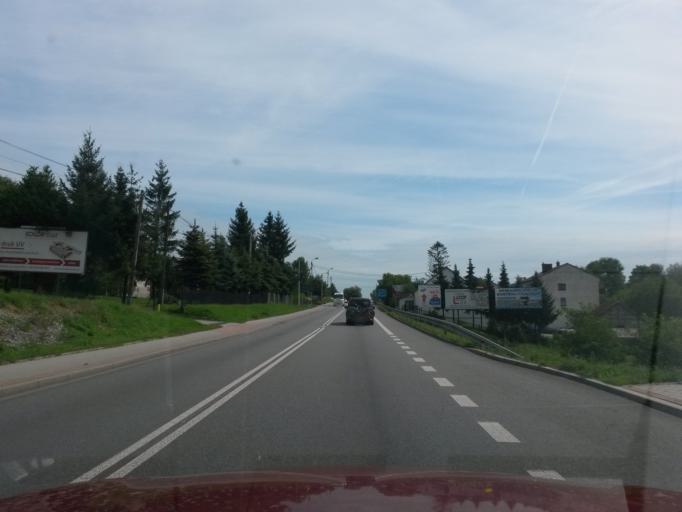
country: PL
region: Lesser Poland Voivodeship
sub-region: Powiat bochenski
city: Lapczyca
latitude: 49.9602
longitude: 20.3962
